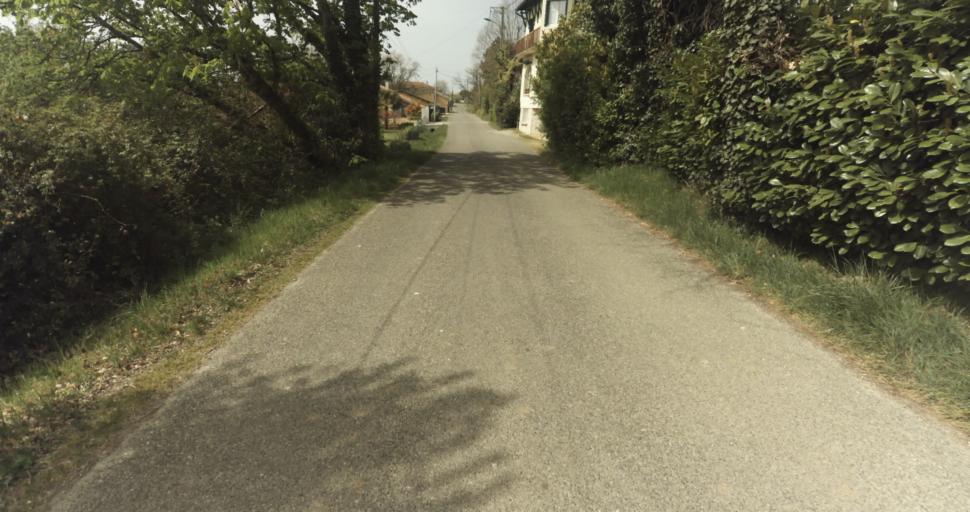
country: FR
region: Midi-Pyrenees
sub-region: Departement du Tarn-et-Garonne
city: Moissac
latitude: 44.1154
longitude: 1.0796
